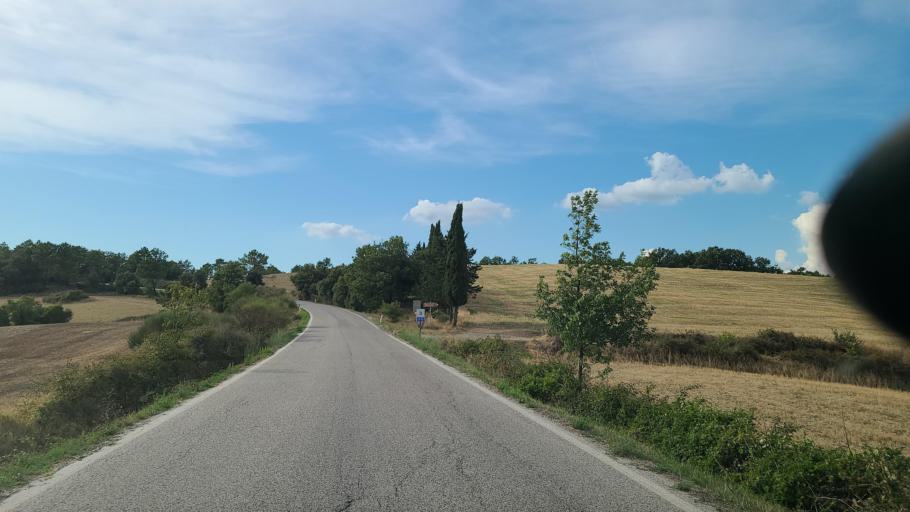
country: IT
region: Tuscany
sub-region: Provincia di Siena
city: San Gimignano
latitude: 43.4271
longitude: 10.9733
